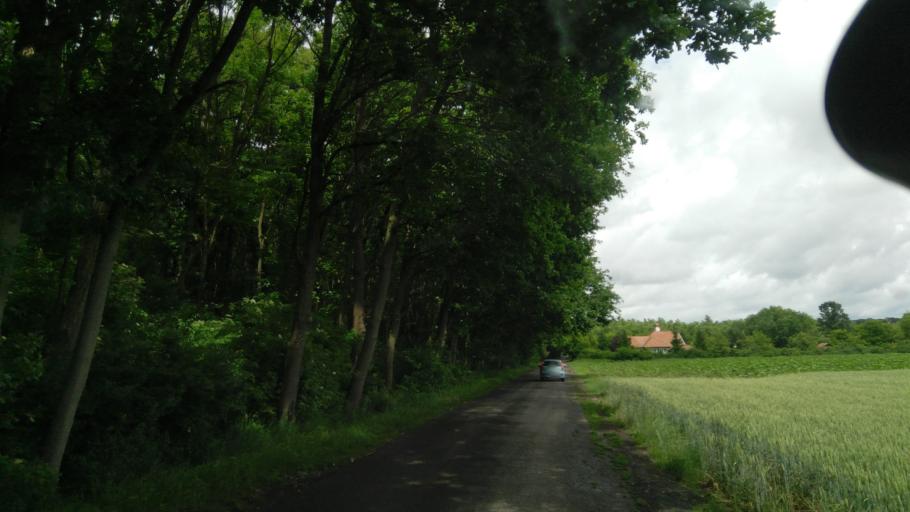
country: HU
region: Bekes
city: Doboz
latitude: 46.6803
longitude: 21.1898
